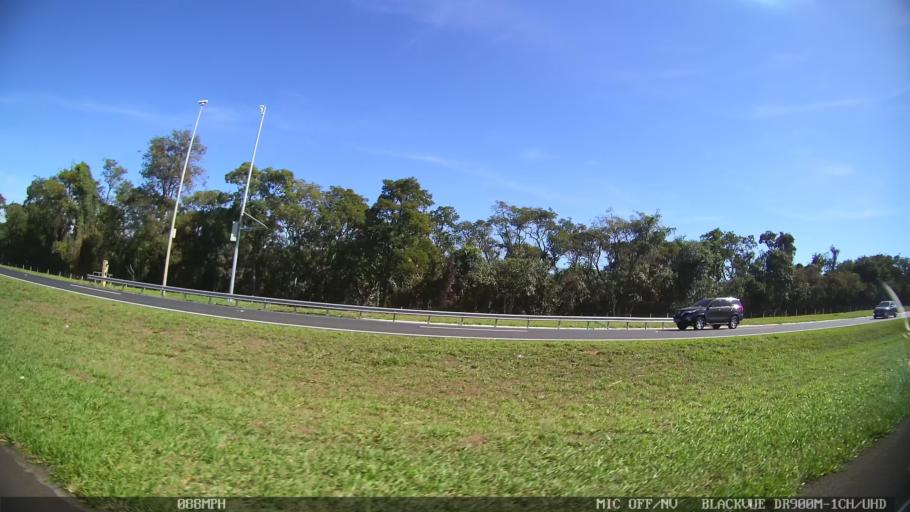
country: BR
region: Sao Paulo
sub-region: Sao Simao
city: Sao Simao
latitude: -21.6225
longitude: -47.6149
